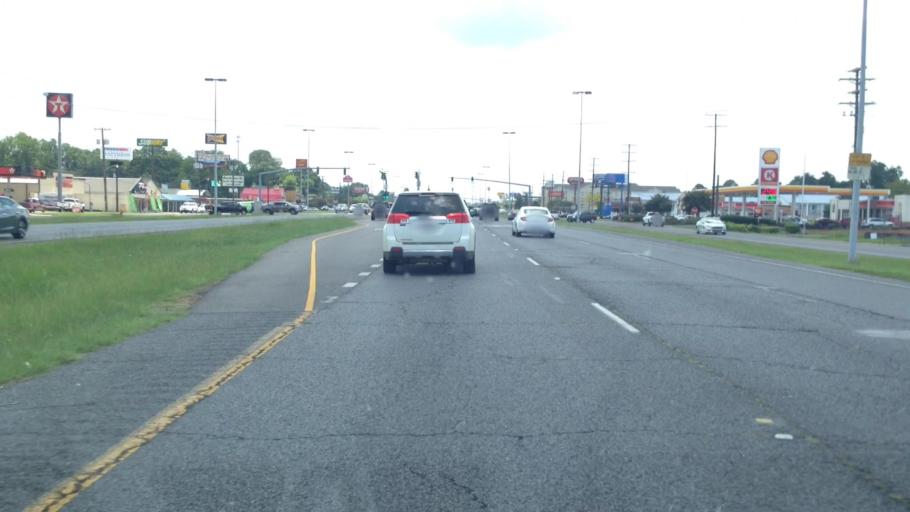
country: US
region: Louisiana
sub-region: Rapides Parish
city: Alexandria
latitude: 31.2965
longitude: -92.4791
